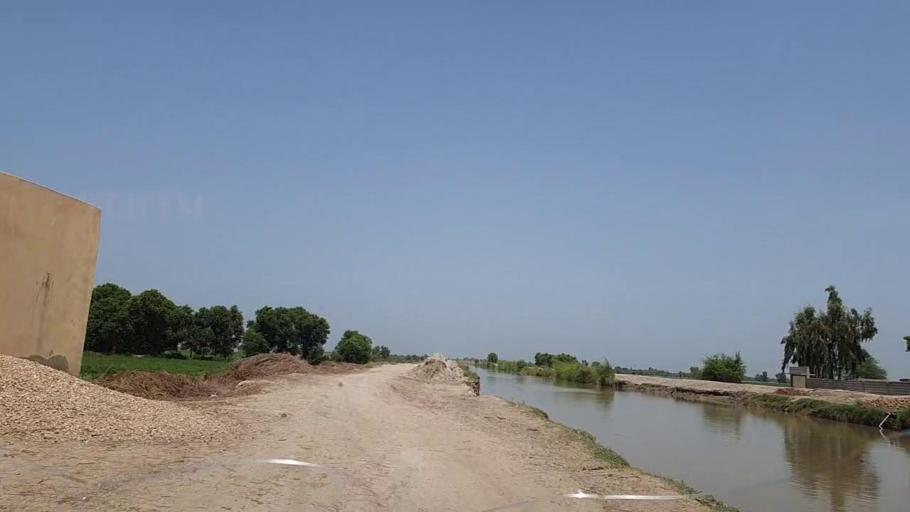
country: PK
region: Sindh
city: Tharu Shah
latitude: 26.9862
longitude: 68.0812
